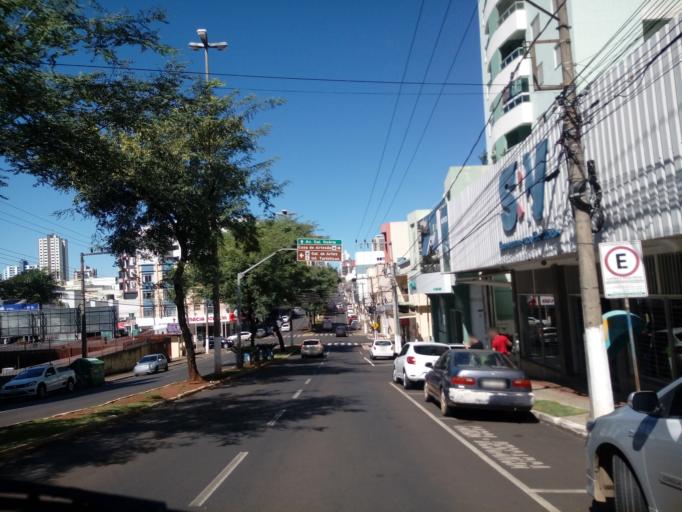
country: BR
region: Santa Catarina
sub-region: Chapeco
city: Chapeco
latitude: -27.0989
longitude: -52.6181
